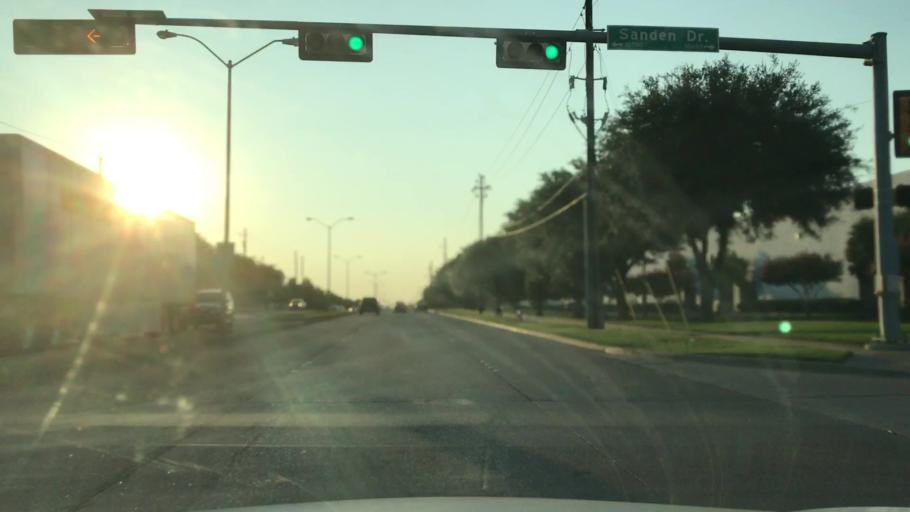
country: US
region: Texas
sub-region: Dallas County
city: Garland
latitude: 32.8945
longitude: -96.6938
